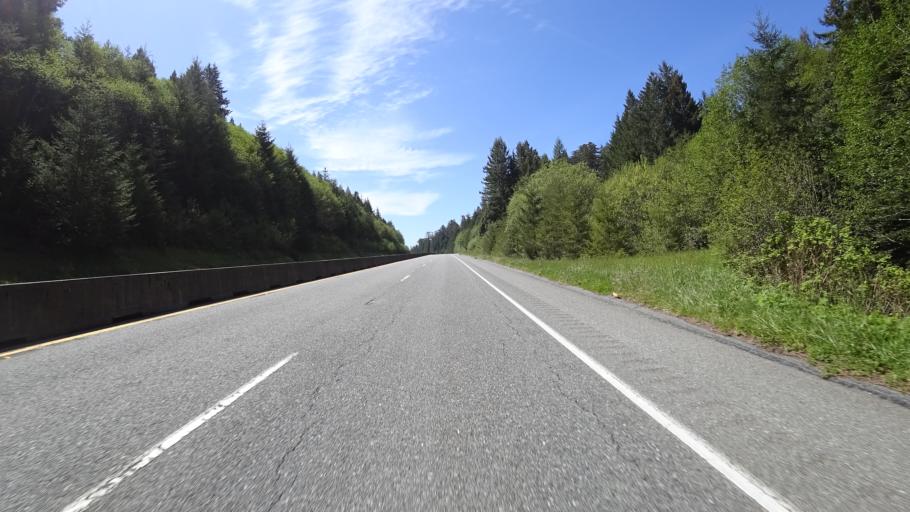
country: US
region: California
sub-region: Humboldt County
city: Westhaven-Moonstone
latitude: 41.3928
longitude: -123.9936
